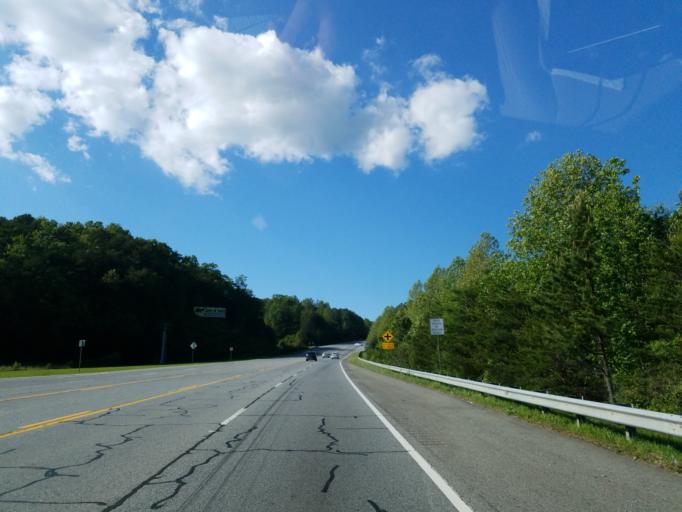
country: US
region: Georgia
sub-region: Fannin County
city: Blue Ridge
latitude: 34.8525
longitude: -84.3370
